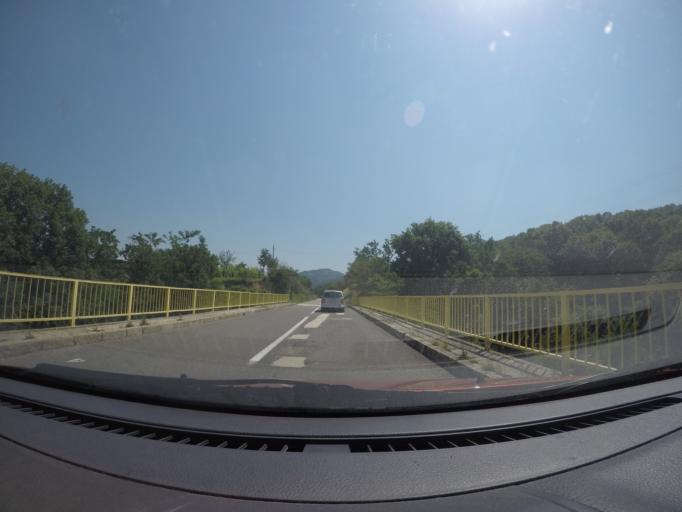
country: RO
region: Mehedinti
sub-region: Comuna Eselnita
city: Eselnita
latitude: 44.6685
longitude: 22.3699
